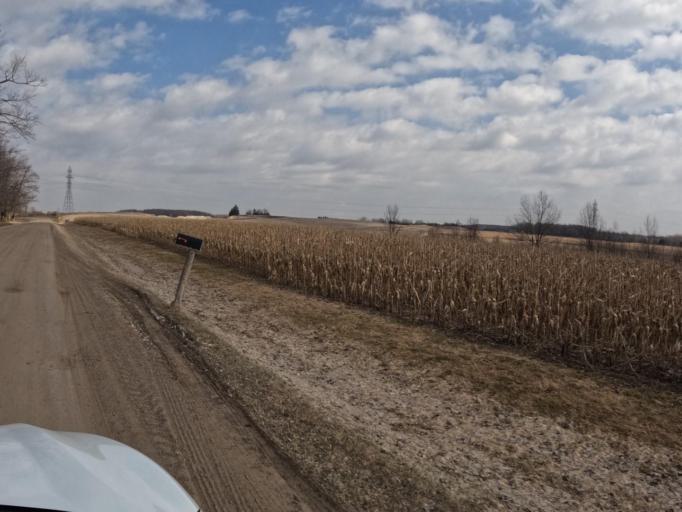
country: CA
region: Ontario
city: Orangeville
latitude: 43.9383
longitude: -80.2433
